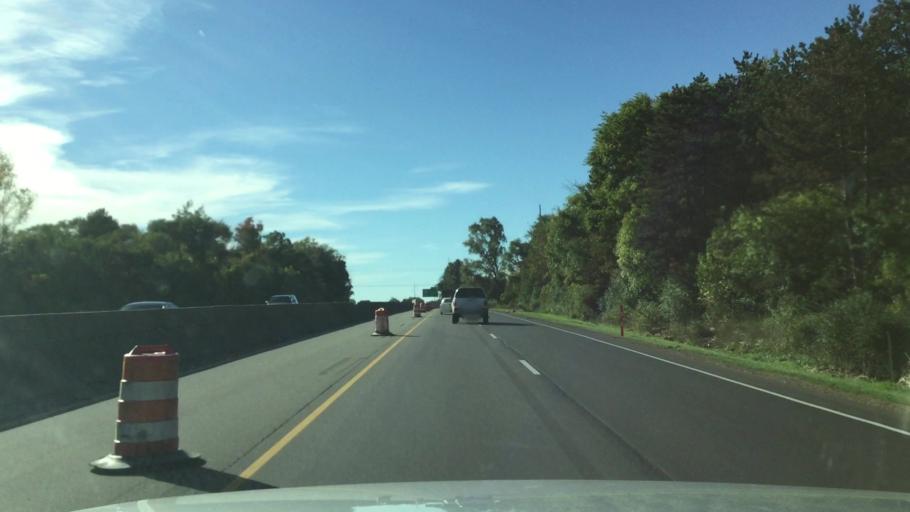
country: US
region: Michigan
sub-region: Jackson County
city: Jackson
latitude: 42.2724
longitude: -84.4170
